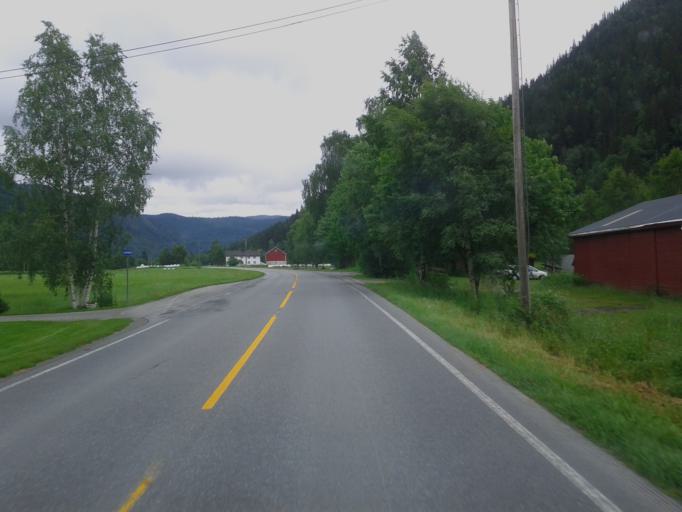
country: NO
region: Sor-Trondelag
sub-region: Midtre Gauldal
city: Storen
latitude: 63.0133
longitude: 10.3660
